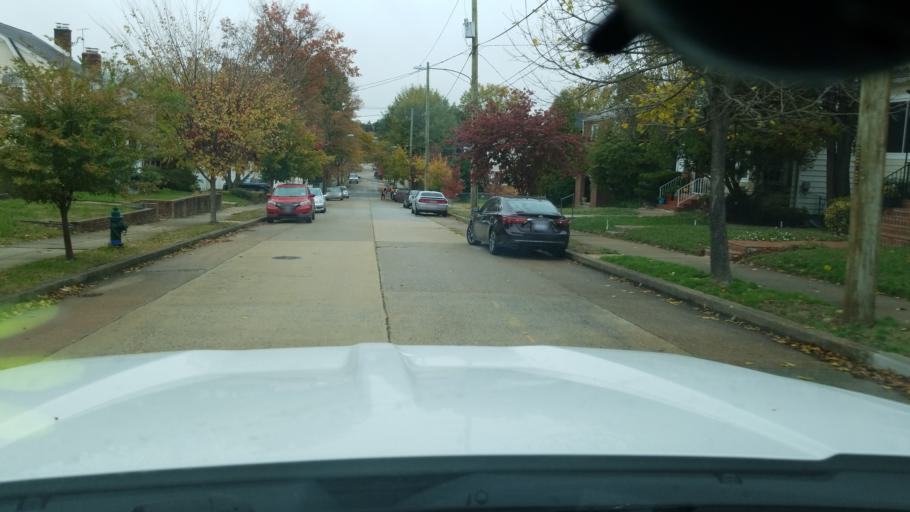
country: US
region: Maryland
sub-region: Prince George's County
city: Mount Rainier
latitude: 38.9372
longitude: -76.9729
